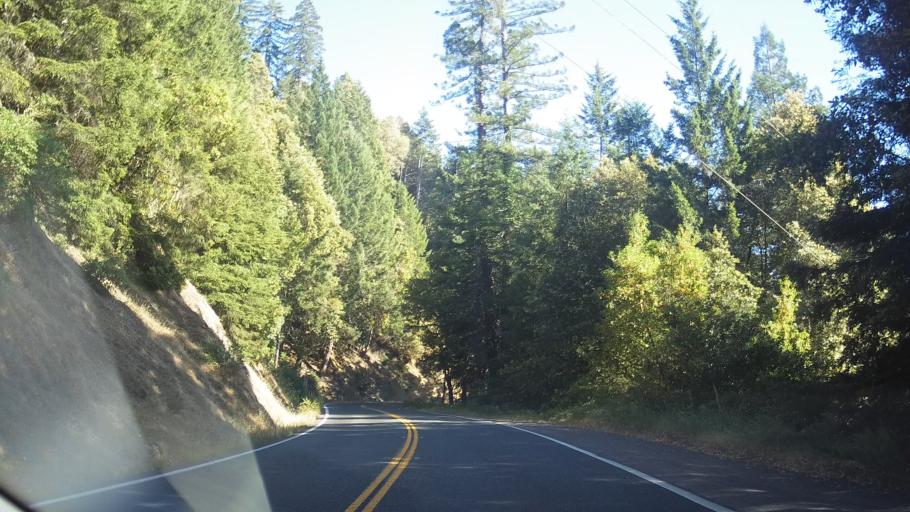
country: US
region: California
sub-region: Mendocino County
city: Brooktrails
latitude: 39.3898
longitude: -123.4677
